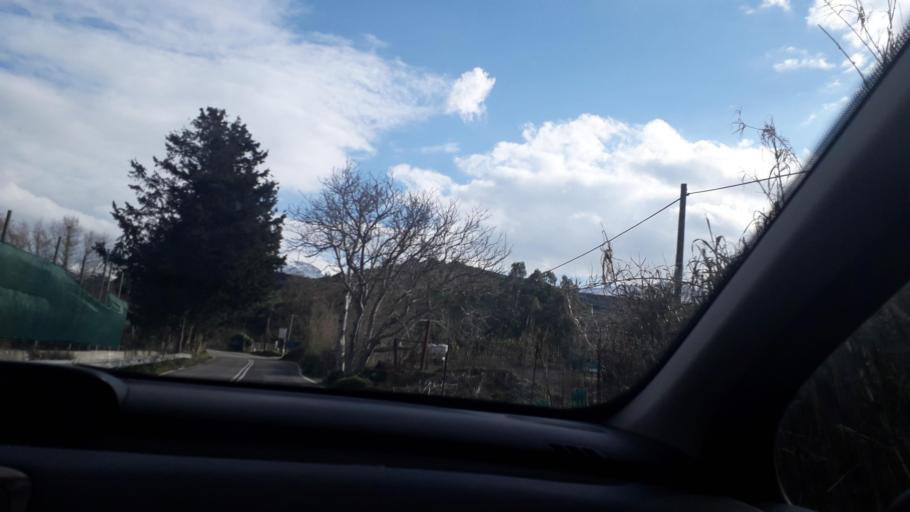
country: GR
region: Crete
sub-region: Nomos Rethymnis
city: Agia Foteini
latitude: 35.2901
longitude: 24.5609
